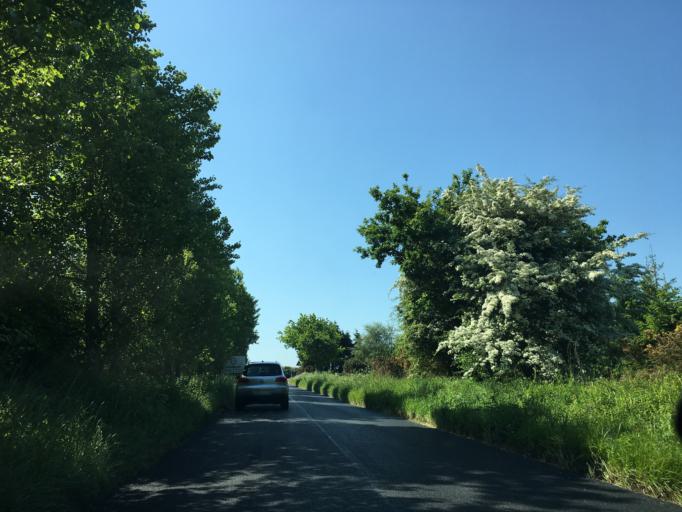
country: GB
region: England
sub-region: Isle of Wight
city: Newchurch
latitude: 50.6493
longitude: -1.2107
